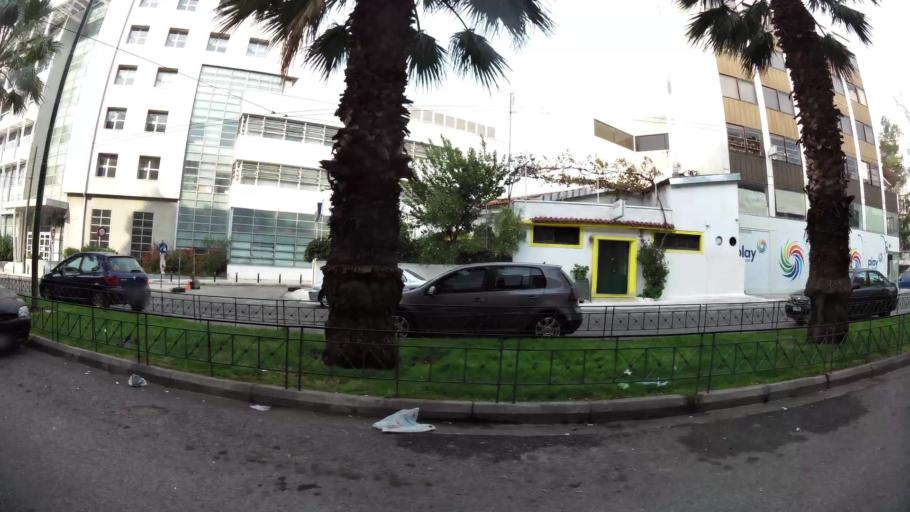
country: GR
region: Attica
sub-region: Nomarchia Athinas
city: Athens
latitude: 37.9955
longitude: 23.7218
